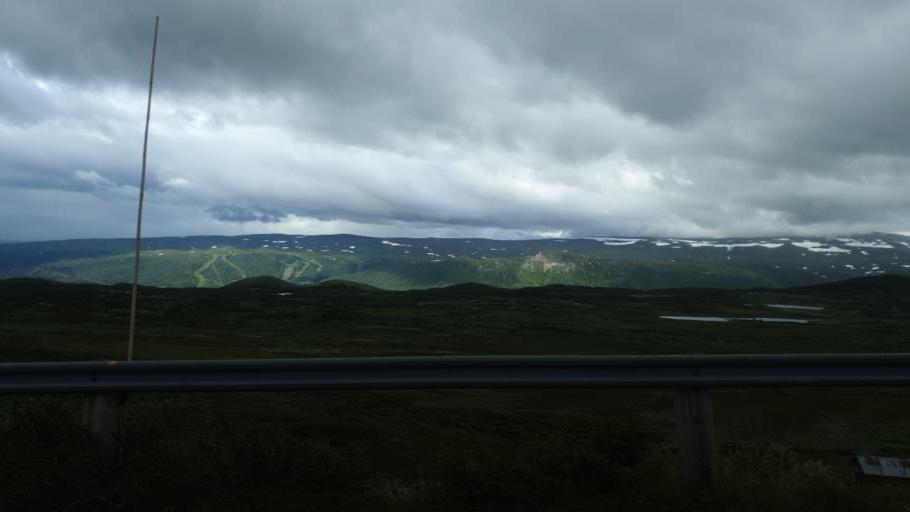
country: NO
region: Oppland
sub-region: Vestre Slidre
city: Slidre
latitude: 61.2782
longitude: 8.8502
